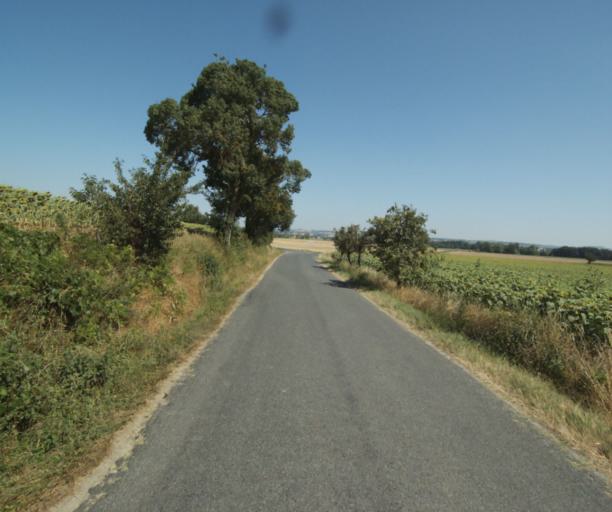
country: FR
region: Midi-Pyrenees
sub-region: Departement de la Haute-Garonne
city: Revel
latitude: 43.5084
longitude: 1.9512
